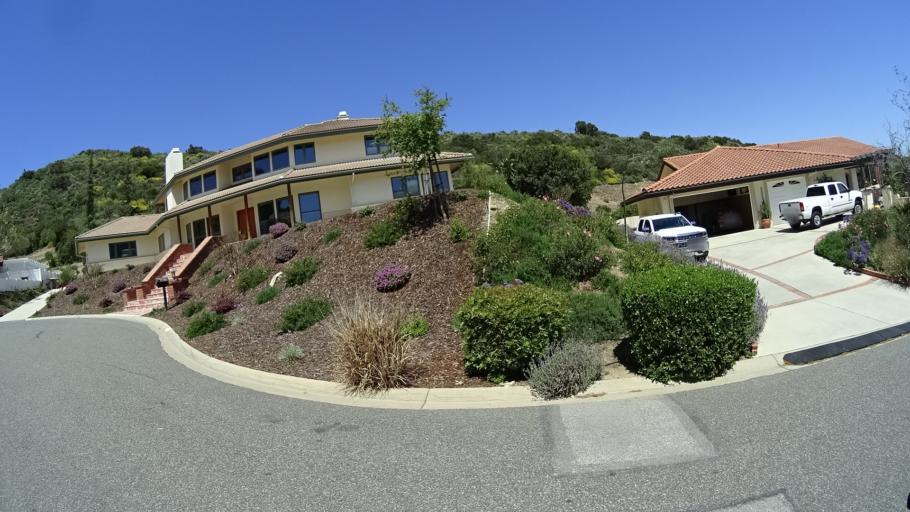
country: US
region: California
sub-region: Ventura County
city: Casa Conejo
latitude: 34.1631
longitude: -118.9636
